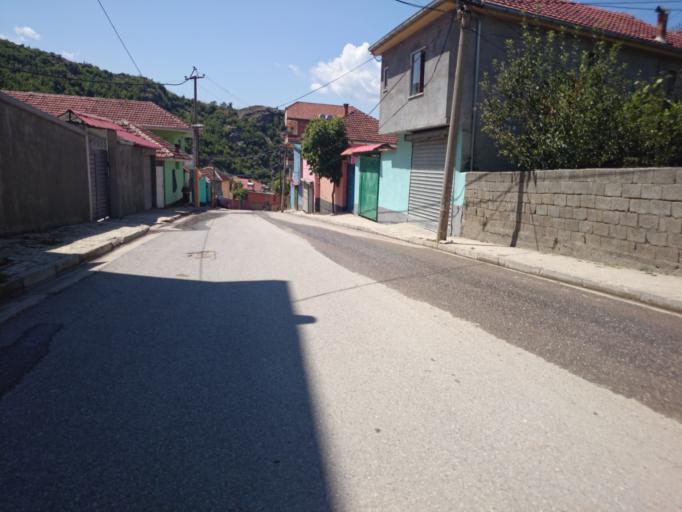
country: AL
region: Diber
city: Peshkopi
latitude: 41.6859
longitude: 20.4463
